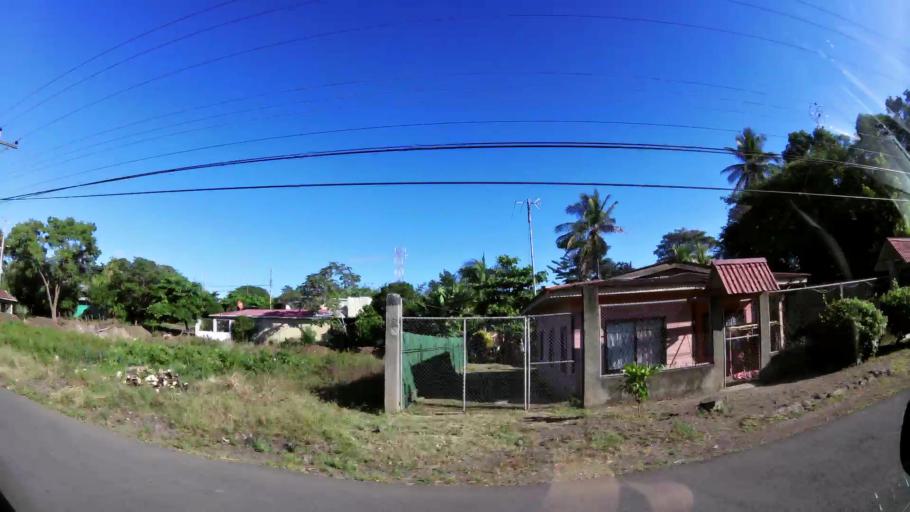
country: CR
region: Guanacaste
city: Sardinal
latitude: 10.4837
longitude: -85.6171
